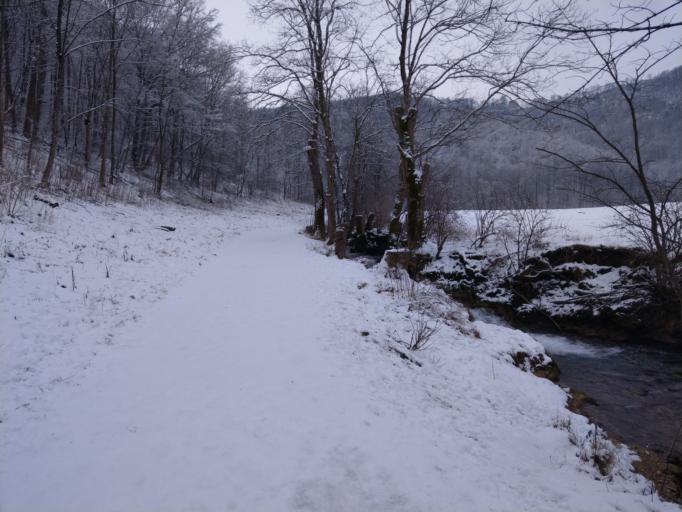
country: DE
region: Baden-Wuerttemberg
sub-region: Tuebingen Region
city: Bad Urach
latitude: 48.4884
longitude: 9.3736
